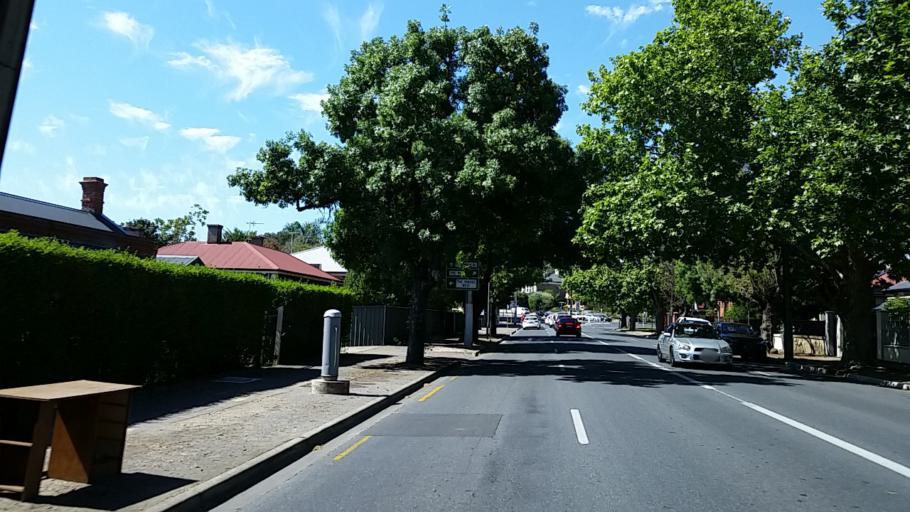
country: AU
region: South Australia
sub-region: Norwood Payneham St Peters
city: Trinity Gardens
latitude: -34.9227
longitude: 138.6219
